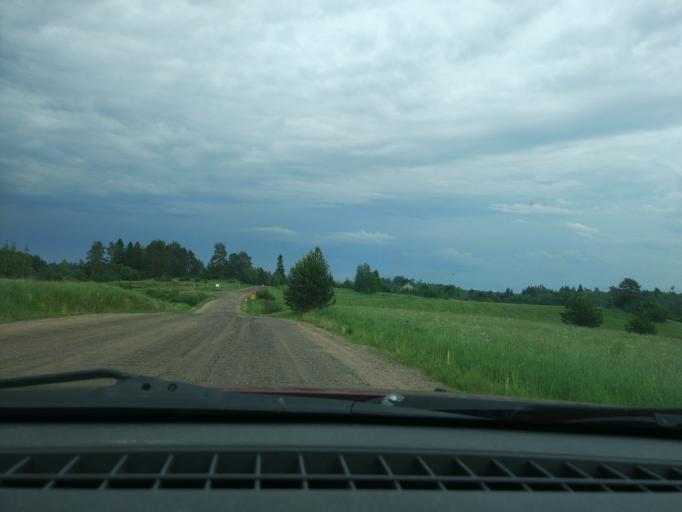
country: RU
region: Leningrad
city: Kuznechnoye
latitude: 61.2868
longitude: 29.8634
